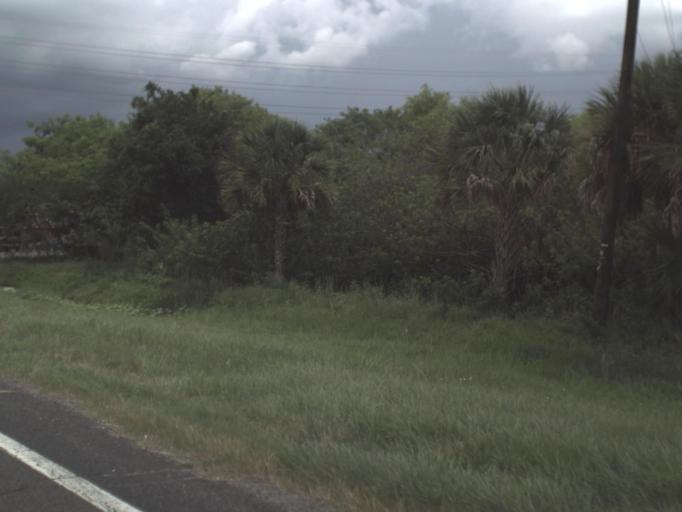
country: US
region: Florida
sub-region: Hillsborough County
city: Palm River-Clair Mel
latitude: 27.9230
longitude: -82.4125
